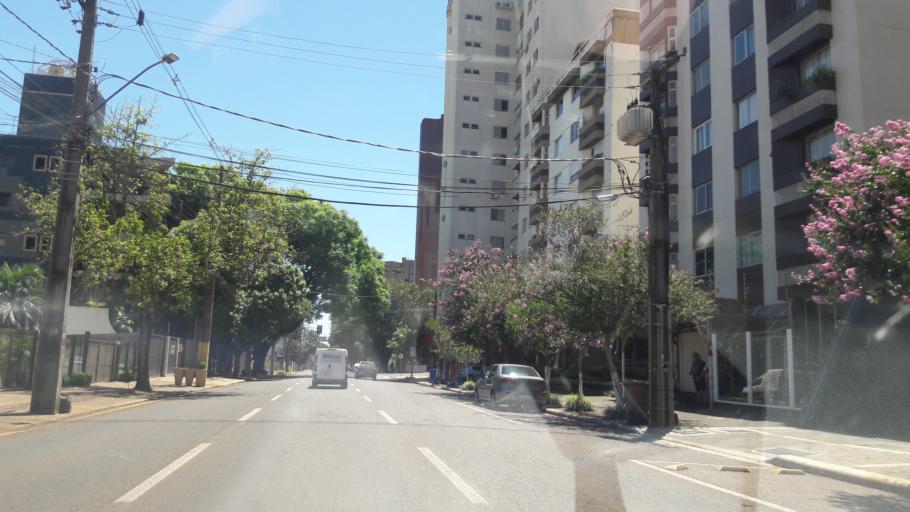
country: BR
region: Parana
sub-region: Cascavel
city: Cascavel
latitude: -24.9525
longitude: -53.4568
